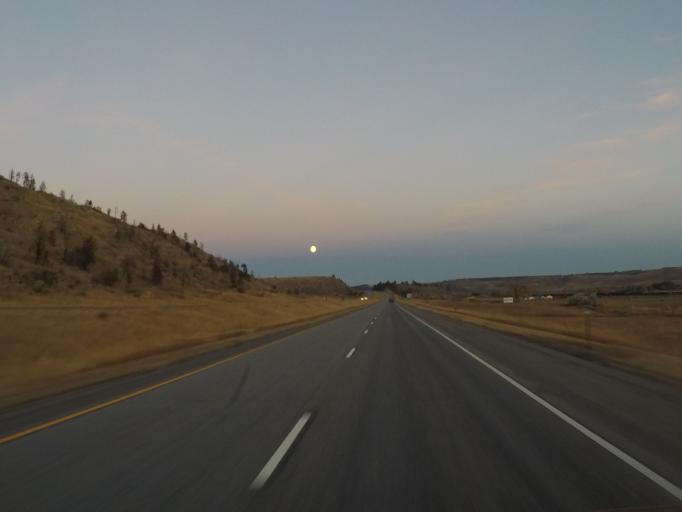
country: US
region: Montana
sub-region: Stillwater County
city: Columbus
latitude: 45.5974
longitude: -109.1071
